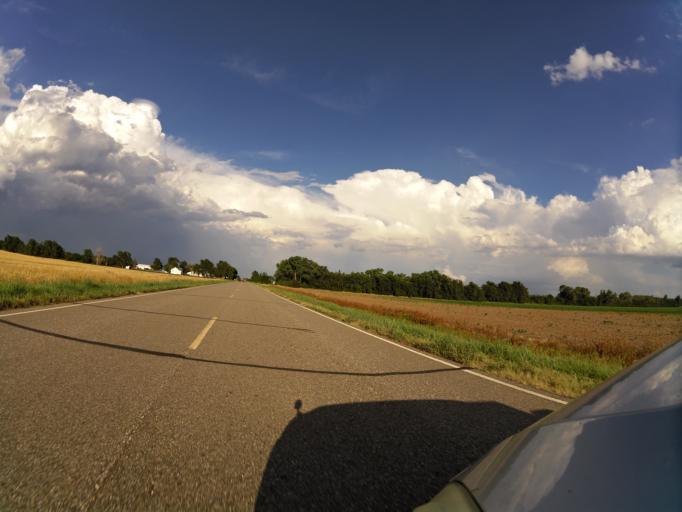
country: US
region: Kansas
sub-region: Reno County
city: South Hutchinson
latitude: 37.9411
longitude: -97.8969
